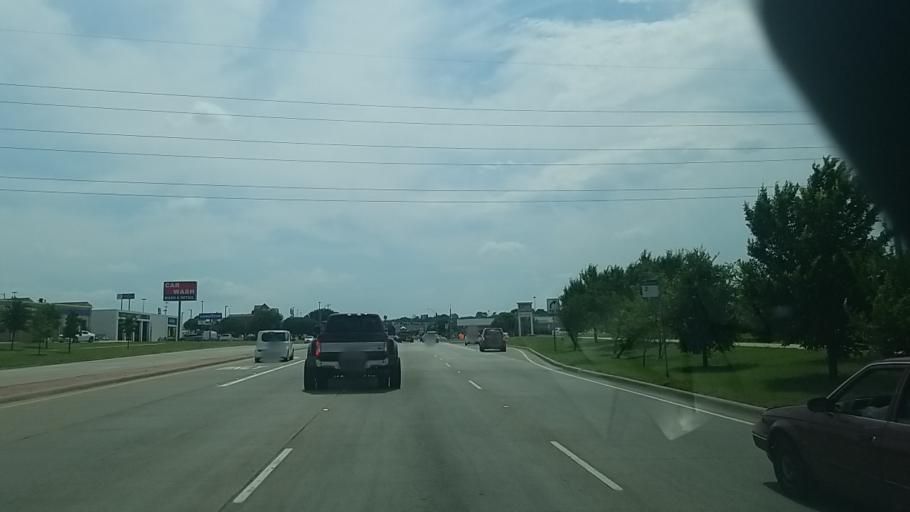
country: US
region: Texas
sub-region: Denton County
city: Denton
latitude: 33.1902
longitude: -97.1021
